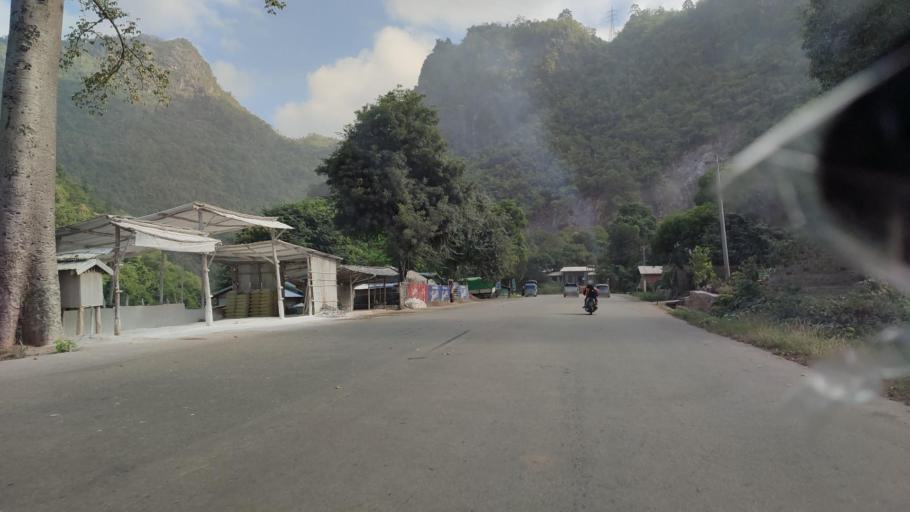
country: MM
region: Mandalay
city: Yamethin
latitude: 20.8226
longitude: 96.4063
